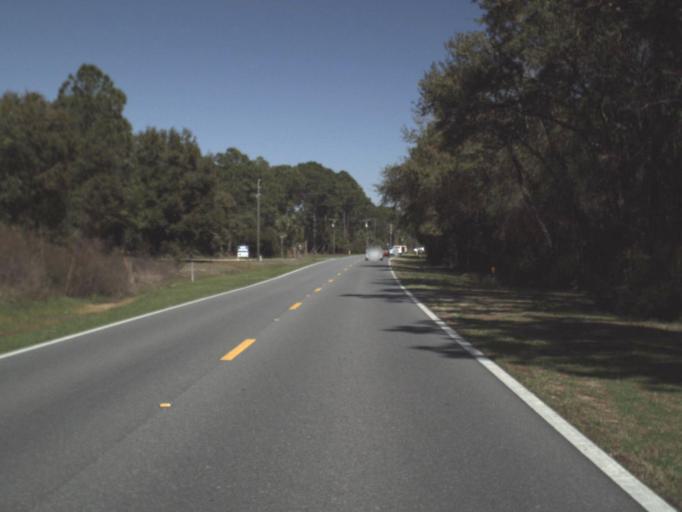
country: US
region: Florida
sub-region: Franklin County
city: Carrabelle
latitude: 29.8871
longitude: -84.5822
